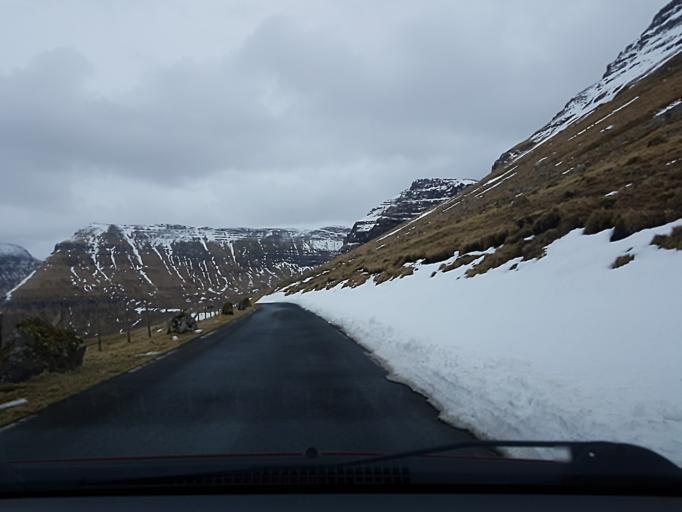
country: FO
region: Streymoy
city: Kollafjordhur
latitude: 62.0110
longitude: -6.9097
